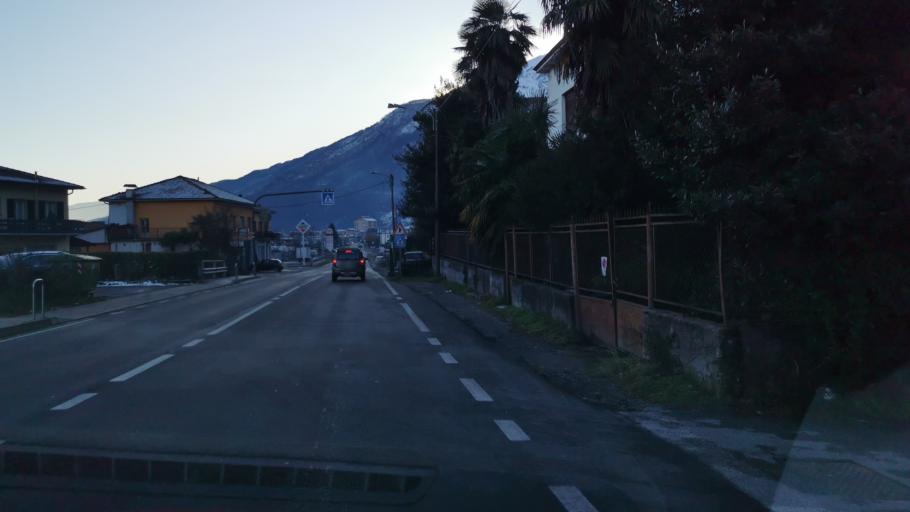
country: IT
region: Lombardy
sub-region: Provincia di Como
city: Consiglio di Rumo
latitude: 46.1395
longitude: 9.2909
